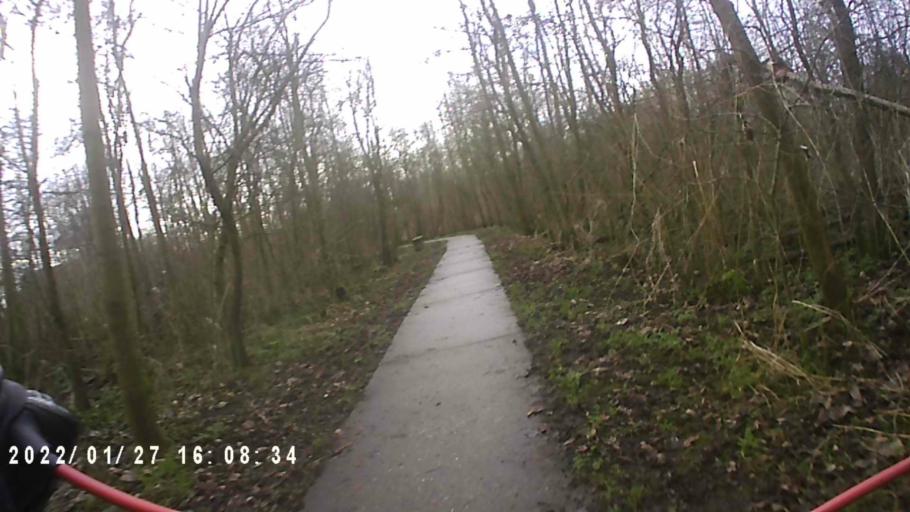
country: NL
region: Friesland
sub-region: Gemeente Dongeradeel
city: Anjum
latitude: 53.3815
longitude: 6.0849
